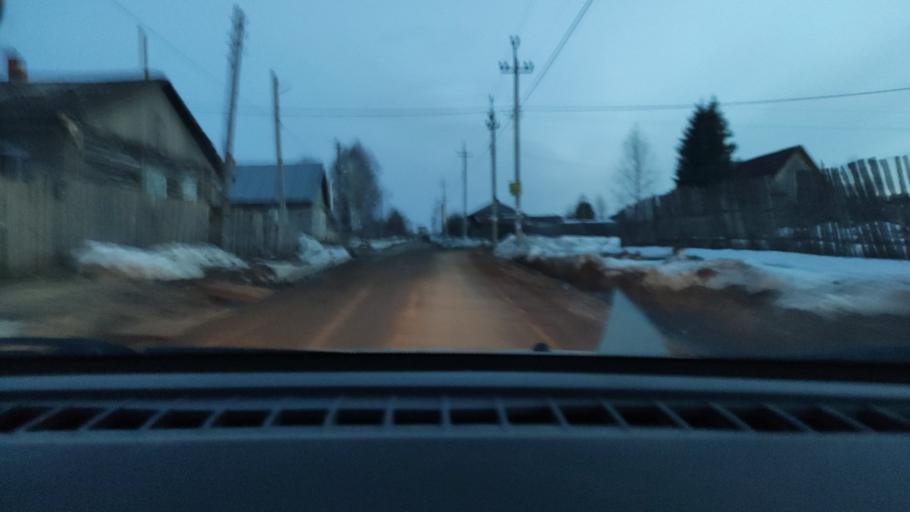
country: RU
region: Perm
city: Yug
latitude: 57.7310
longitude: 56.1679
